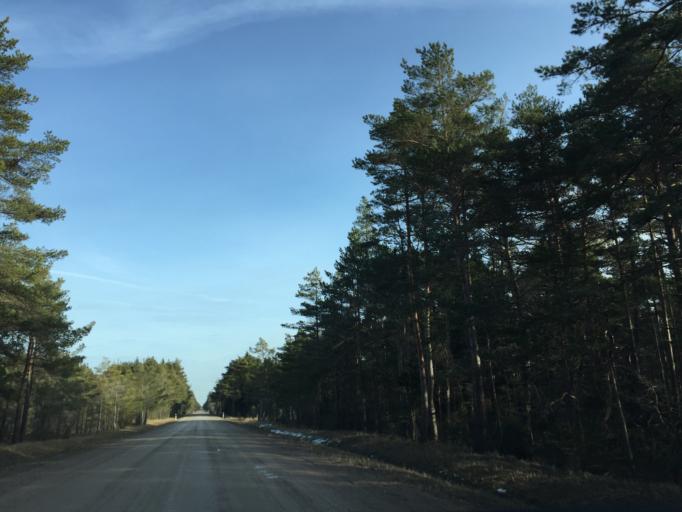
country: EE
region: Saare
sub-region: Kuressaare linn
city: Kuressaare
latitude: 58.3015
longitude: 21.9594
